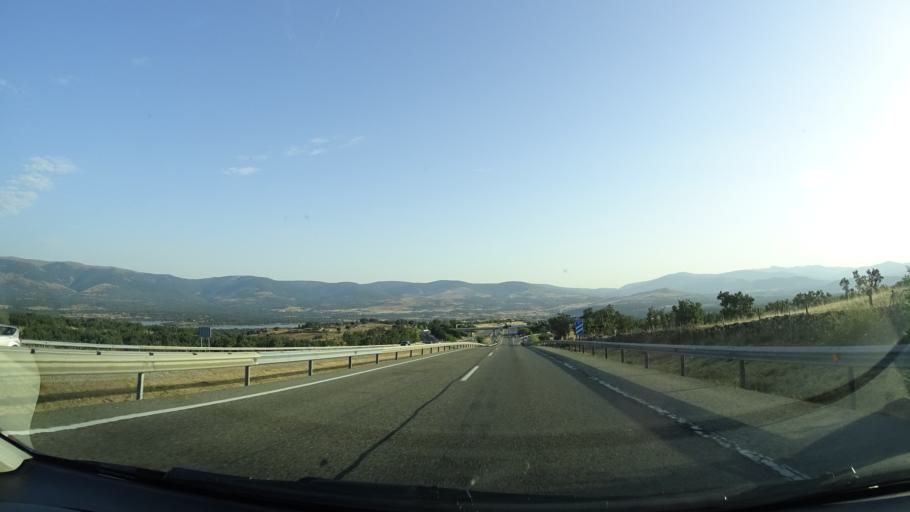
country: ES
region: Madrid
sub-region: Provincia de Madrid
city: Buitrago del Lozoya
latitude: 40.9610
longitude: -3.6413
